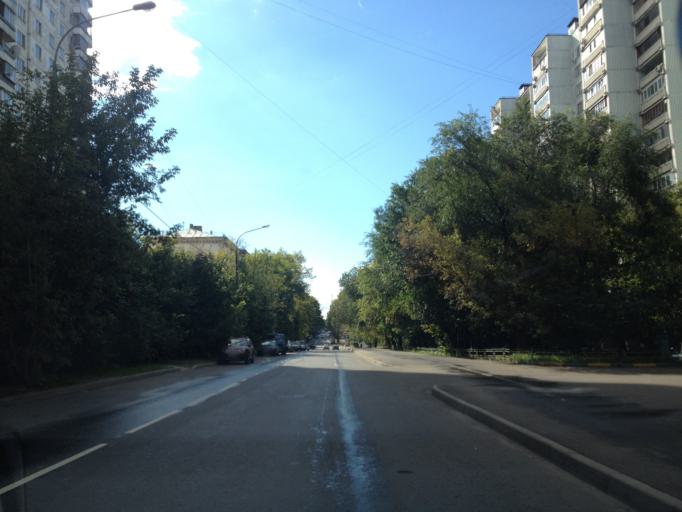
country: RU
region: Moscow
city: Metrogorodok
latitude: 55.7988
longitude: 37.7937
